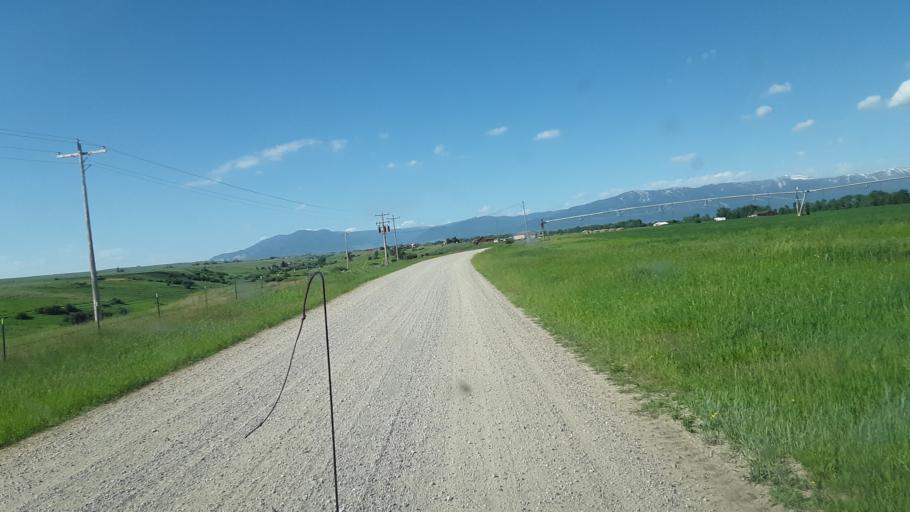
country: US
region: Montana
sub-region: Carbon County
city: Red Lodge
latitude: 45.3309
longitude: -109.1666
